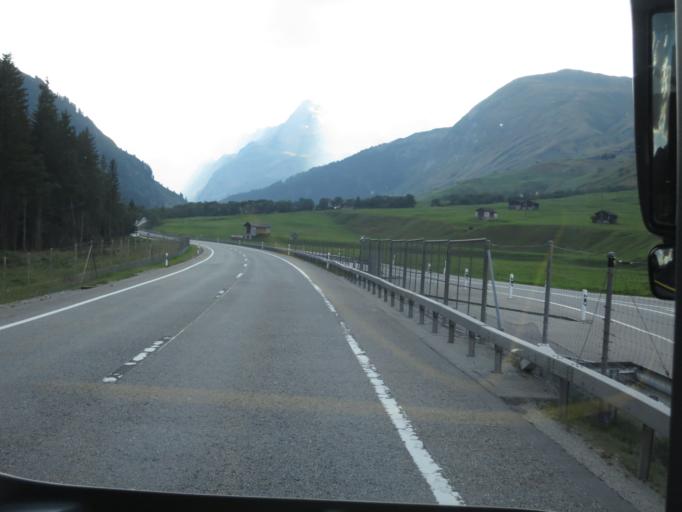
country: CH
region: Grisons
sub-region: Hinterrhein District
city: Hinterrhein
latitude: 46.5411
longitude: 9.2646
